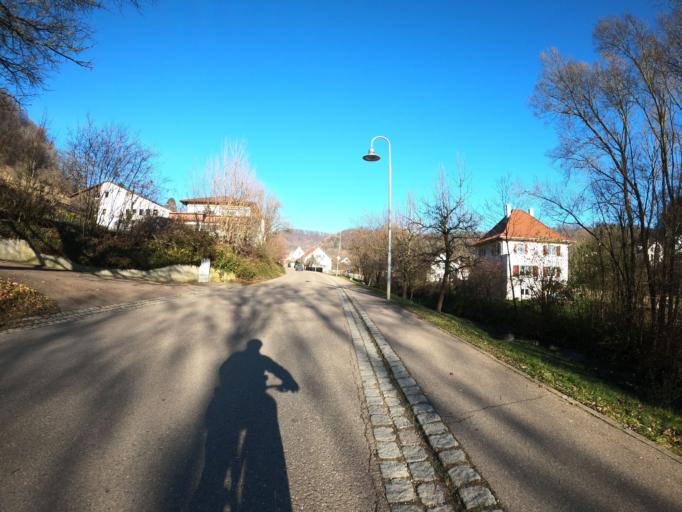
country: DE
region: Baden-Wuerttemberg
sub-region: Regierungsbezirk Stuttgart
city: Bad Ditzenbach
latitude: 48.6143
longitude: 9.6789
